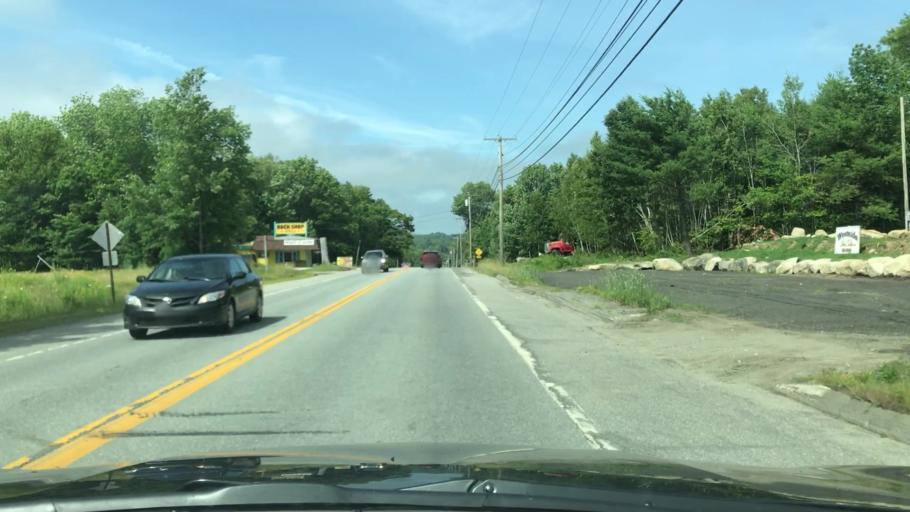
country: US
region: Maine
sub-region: Hancock County
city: Bucksport
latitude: 44.5595
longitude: -68.7930
